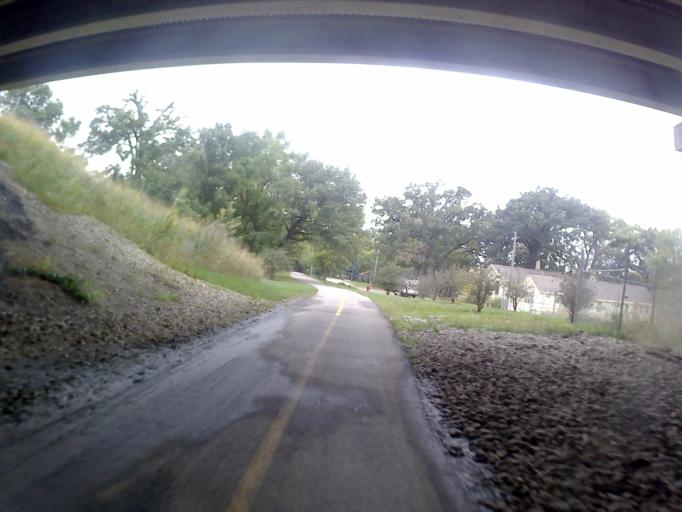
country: US
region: Illinois
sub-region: Kane County
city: North Aurora
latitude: 41.7962
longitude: -88.3219
